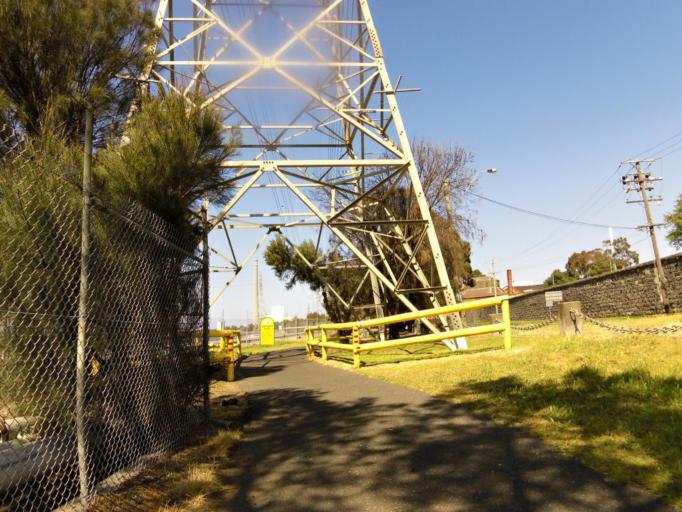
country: AU
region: Victoria
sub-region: Hobsons Bay
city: Spotswood
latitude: -37.8297
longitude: 144.8960
